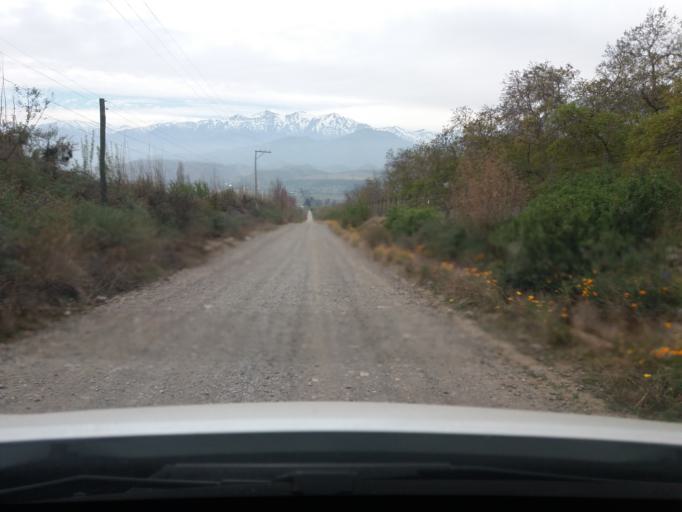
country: CL
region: Valparaiso
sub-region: Provincia de Los Andes
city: Los Andes
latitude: -32.8456
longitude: -70.5536
